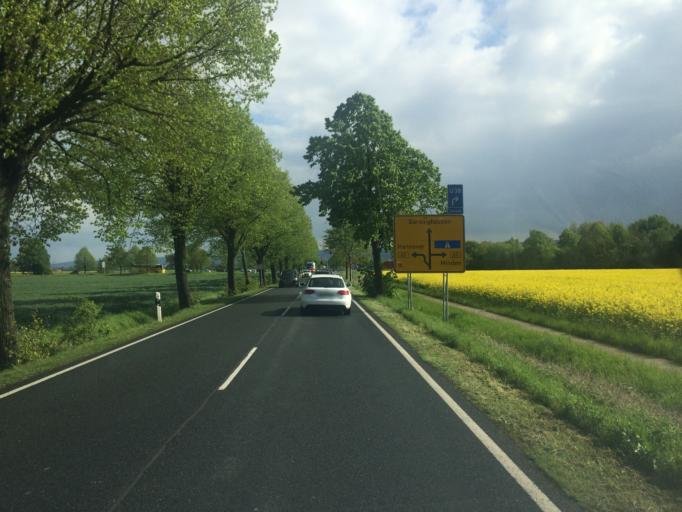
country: DE
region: Lower Saxony
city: Gross Munzel
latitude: 52.3348
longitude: 9.4663
